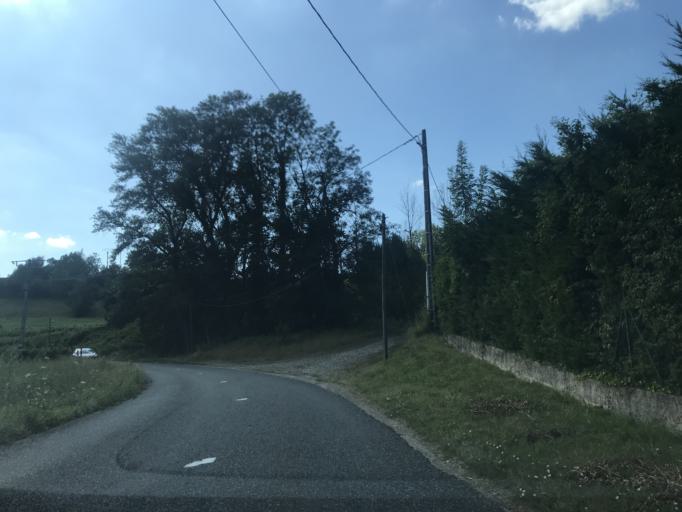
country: FR
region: Rhone-Alpes
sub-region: Departement de la Savoie
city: Yenne
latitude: 45.7177
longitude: 5.8181
